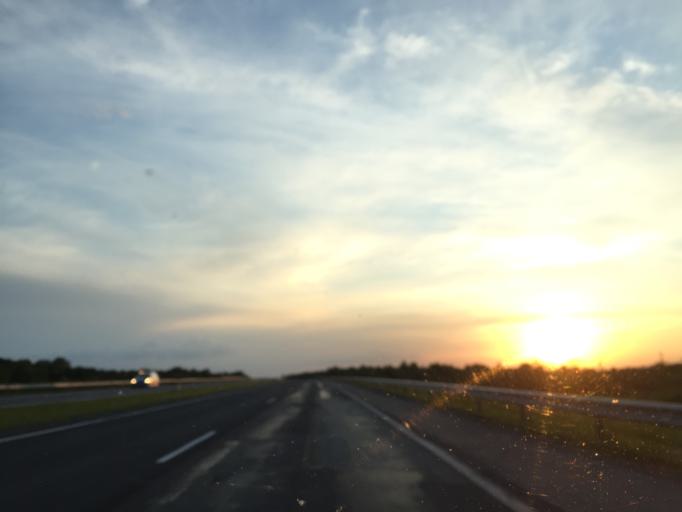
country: LT
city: Kursenai
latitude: 55.9884
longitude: 23.0741
